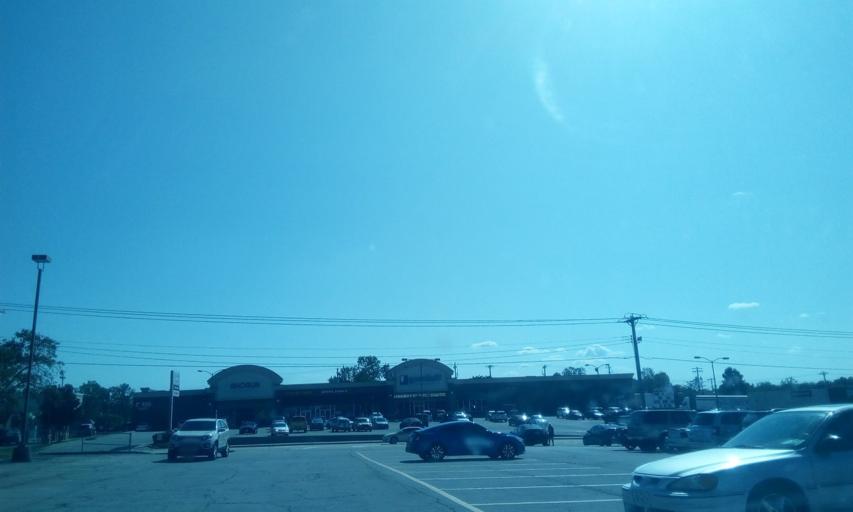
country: US
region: Missouri
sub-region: Saint Louis County
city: Concord
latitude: 38.5244
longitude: -90.3622
